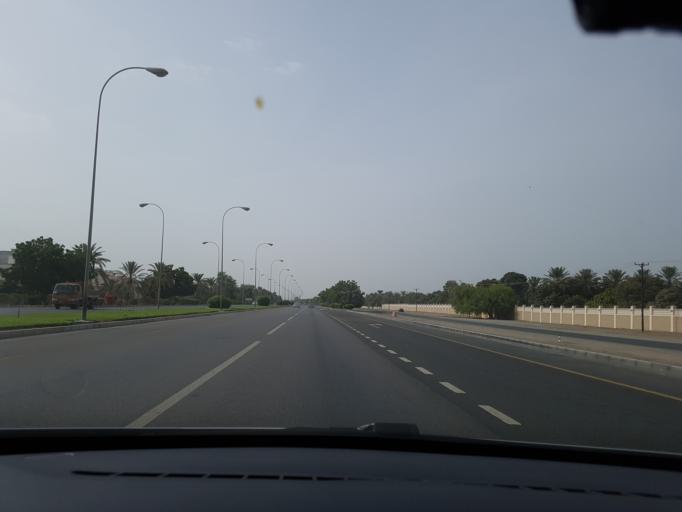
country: OM
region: Al Batinah
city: Al Sohar
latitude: 24.3792
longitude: 56.7025
